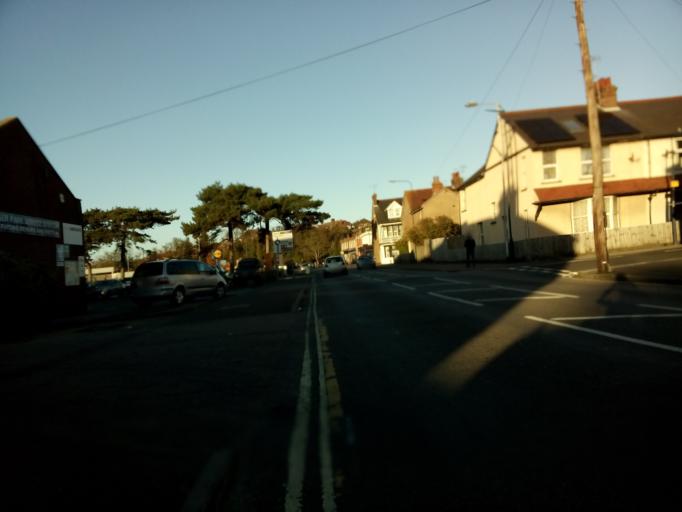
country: GB
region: England
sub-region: Suffolk
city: Felixstowe
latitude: 51.9568
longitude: 1.3398
